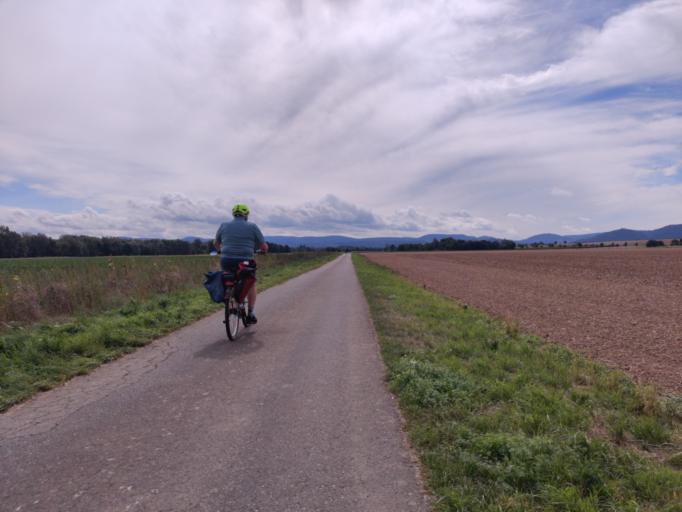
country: DE
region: Lower Saxony
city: Liebenburg
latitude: 51.9964
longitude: 10.3708
